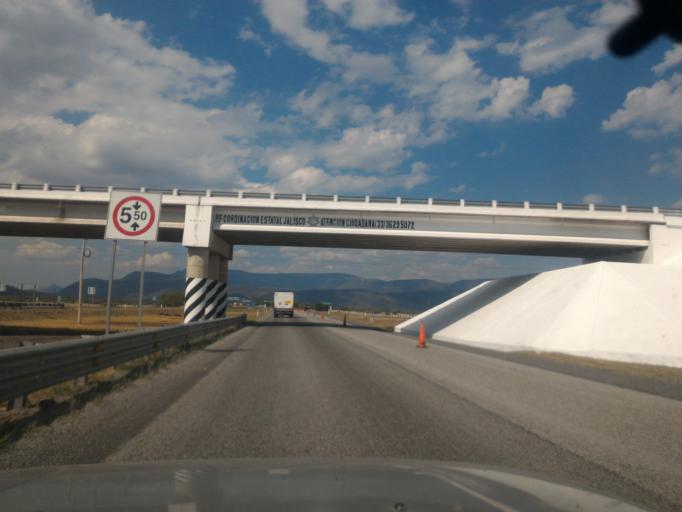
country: MX
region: Jalisco
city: Zacoalco de Torres
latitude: 20.1299
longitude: -103.5073
